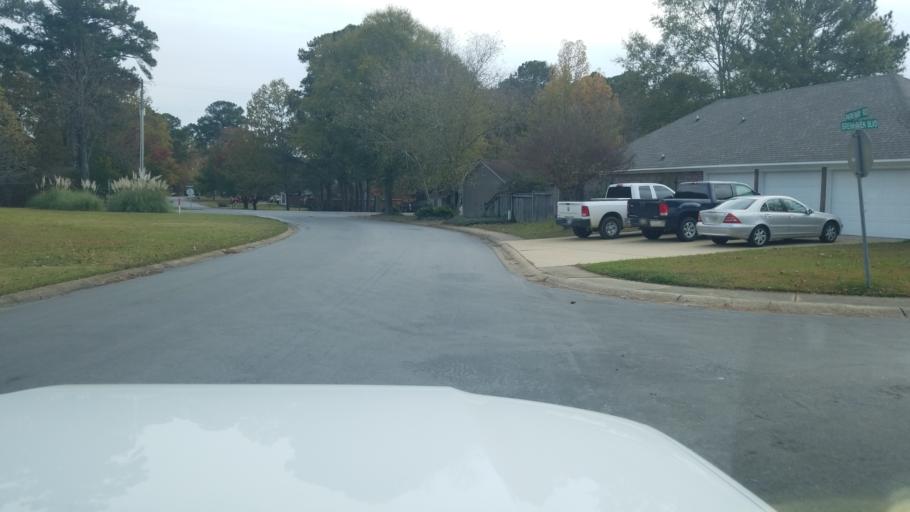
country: US
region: Mississippi
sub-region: Madison County
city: Ridgeland
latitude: 32.3877
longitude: -90.0353
